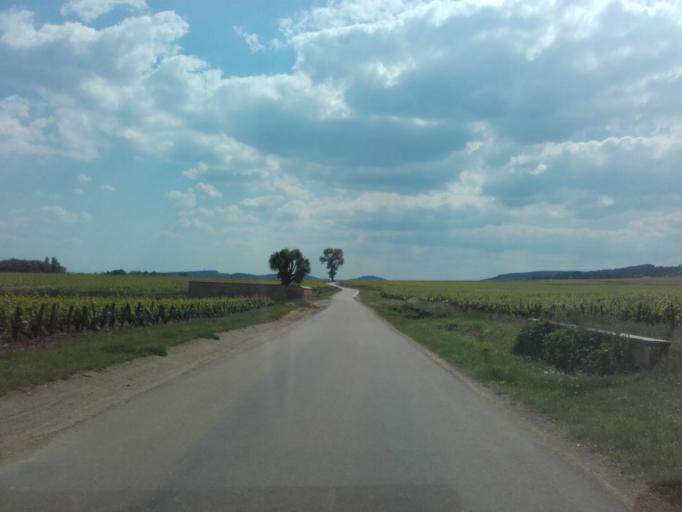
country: FR
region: Bourgogne
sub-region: Departement de la Cote-d'Or
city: Meursault
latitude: 46.9648
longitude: 4.7628
